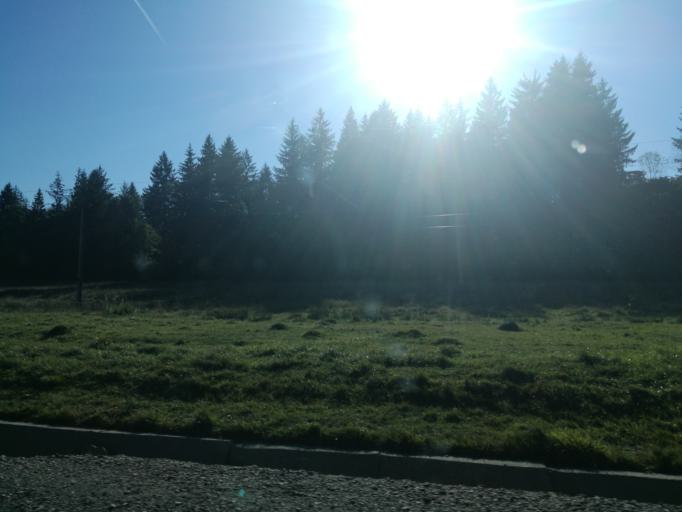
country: RO
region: Brasov
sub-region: Comuna Dumbravita
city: Dumbravita
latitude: 45.7593
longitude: 25.3857
